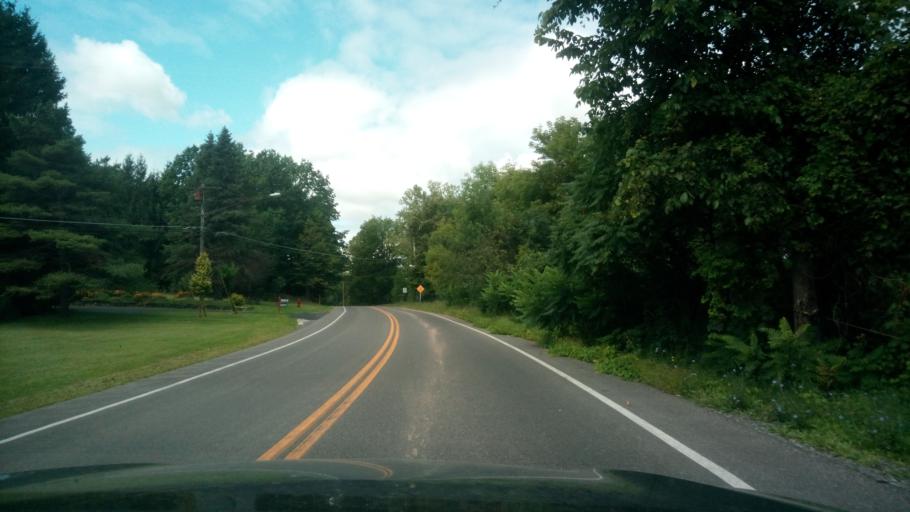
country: US
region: New York
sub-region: Onondaga County
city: East Syracuse
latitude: 43.0051
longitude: -76.0833
